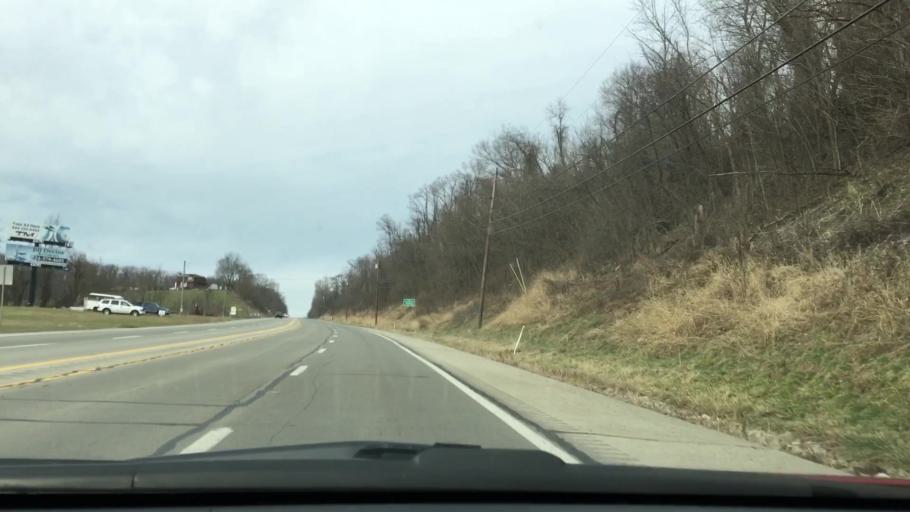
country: US
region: Pennsylvania
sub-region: Fayette County
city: Perryopolis
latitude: 40.0978
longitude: -79.7635
